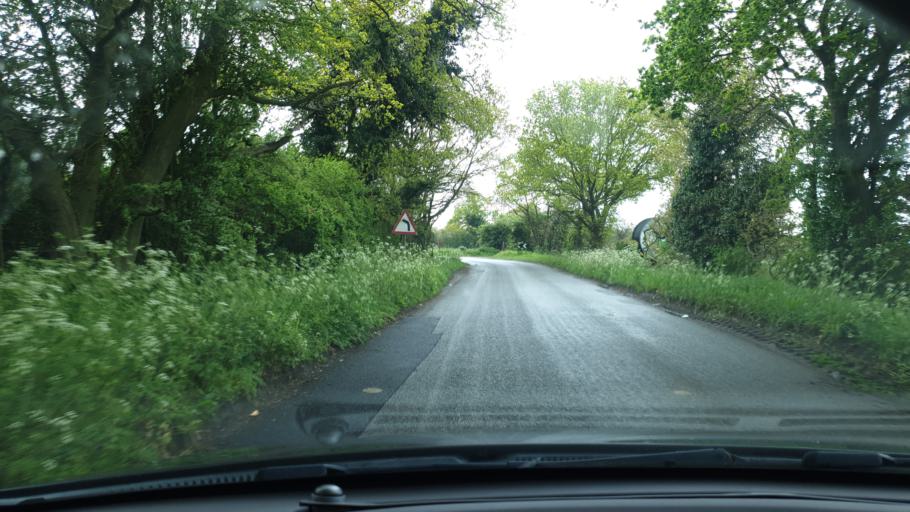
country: GB
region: England
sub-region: Essex
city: Wivenhoe
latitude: 51.8954
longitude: 0.9672
